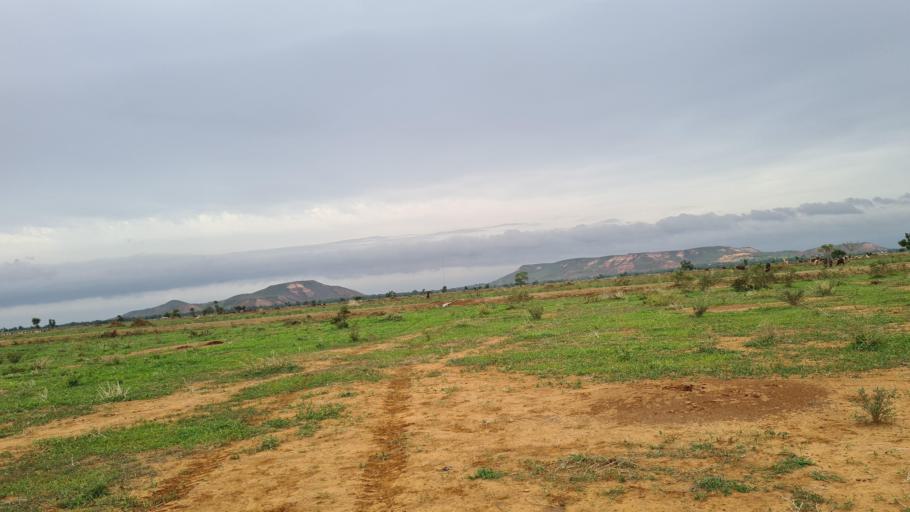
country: NE
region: Tahoua
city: Birni N Konni
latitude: 13.8413
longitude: 5.2710
